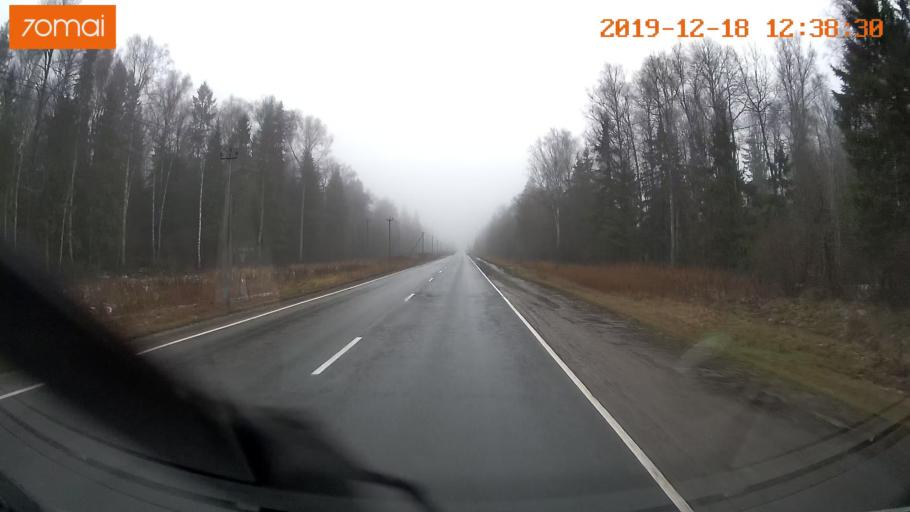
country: RU
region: Moskovskaya
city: Vysokovsk
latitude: 56.1525
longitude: 36.6053
